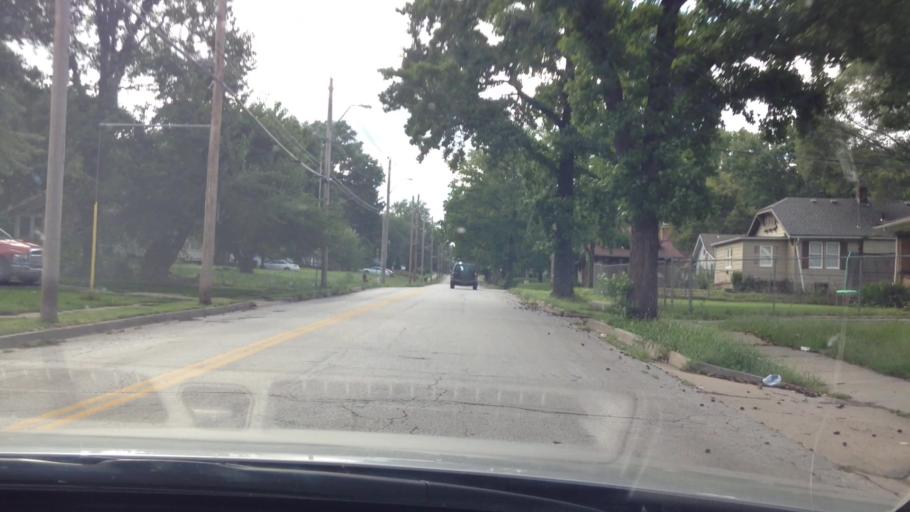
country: US
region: Kansas
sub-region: Johnson County
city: Mission Hills
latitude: 39.0195
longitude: -94.5617
